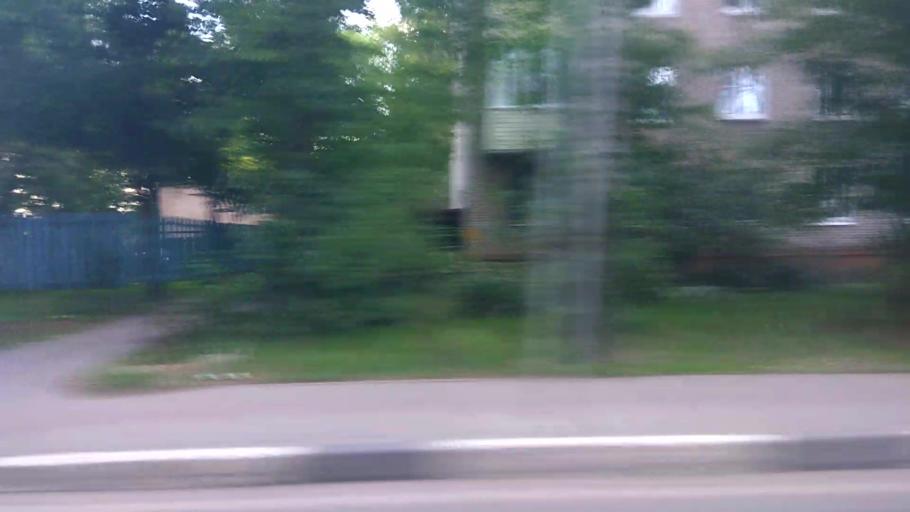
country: RU
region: Moskovskaya
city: Korolev
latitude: 55.9224
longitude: 37.7837
